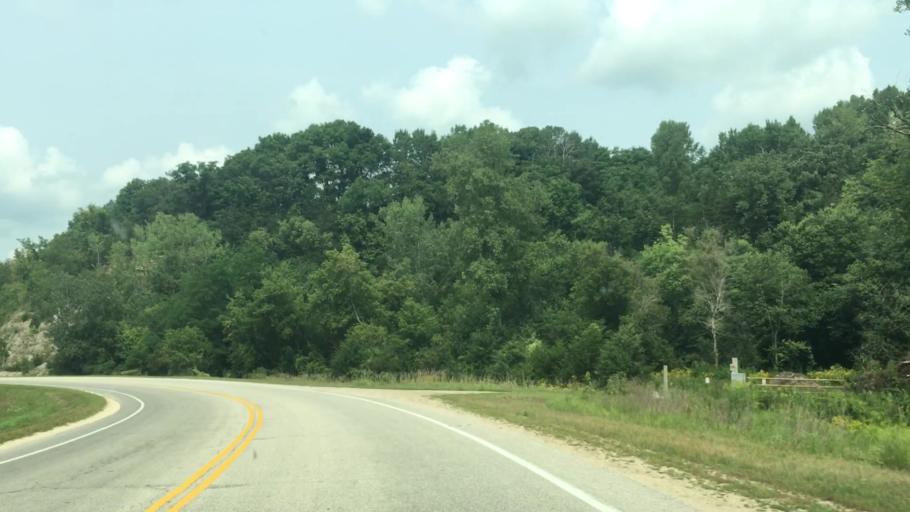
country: US
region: Minnesota
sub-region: Fillmore County
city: Preston
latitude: 43.7059
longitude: -91.9713
